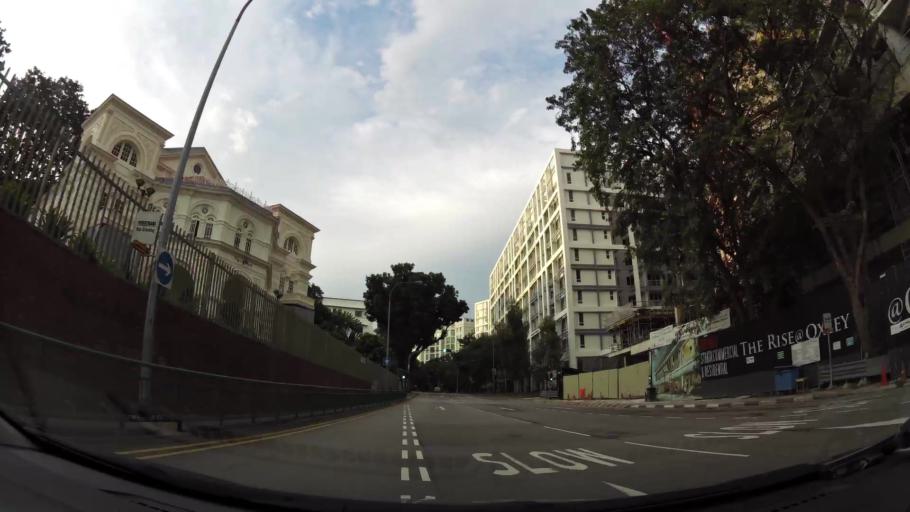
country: SG
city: Singapore
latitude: 1.2972
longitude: 103.8430
